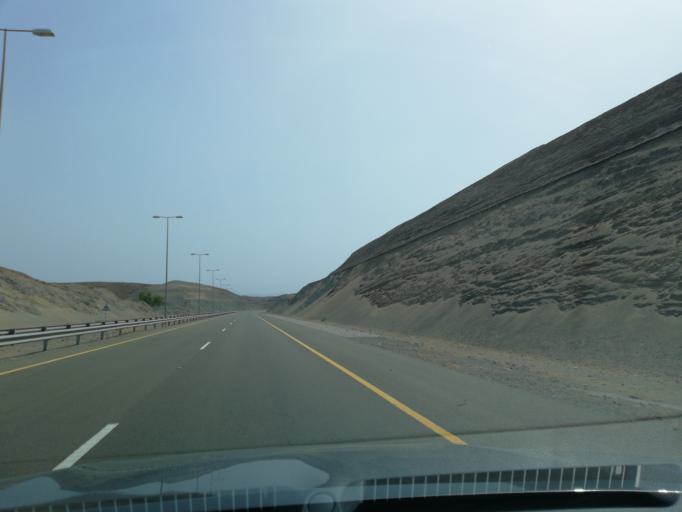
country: OM
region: Al Batinah
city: Al Liwa'
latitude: 24.3114
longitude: 56.4485
